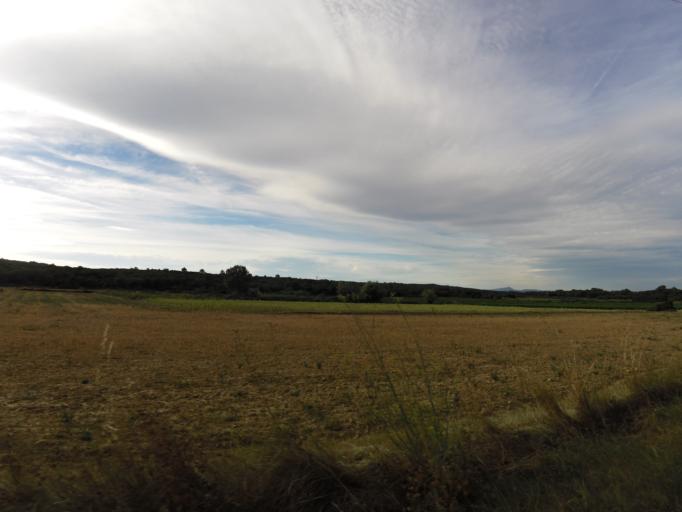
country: FR
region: Languedoc-Roussillon
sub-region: Departement du Gard
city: Saint-Mamert-du-Gard
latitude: 43.8748
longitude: 4.1743
